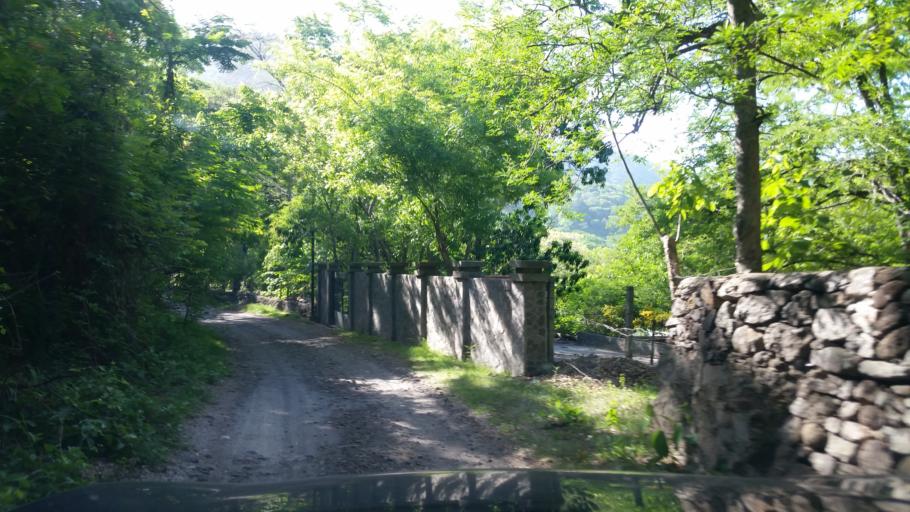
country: NI
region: Masaya
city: Catarina
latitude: 11.9112
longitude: -86.0558
